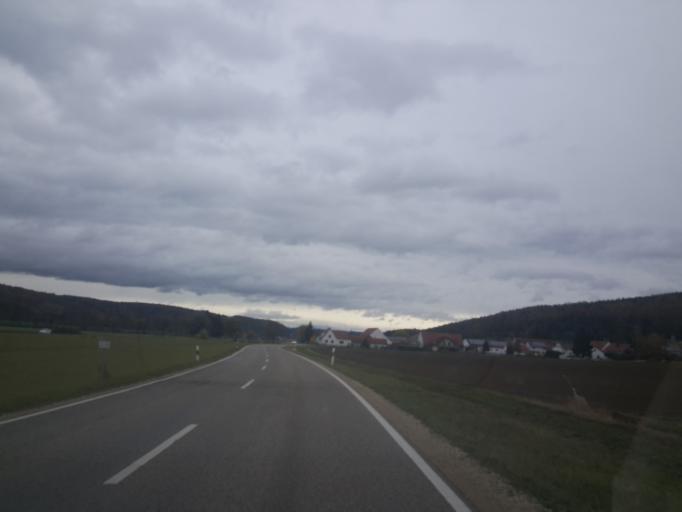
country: DE
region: Bavaria
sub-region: Upper Bavaria
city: Rennertshofen
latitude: 48.7809
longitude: 11.0703
